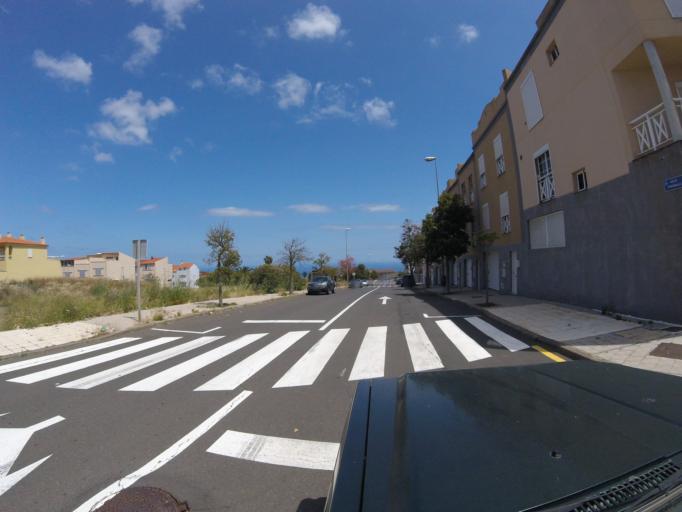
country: ES
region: Canary Islands
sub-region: Provincia de Santa Cruz de Tenerife
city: La Laguna
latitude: 28.4455
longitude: -16.3138
